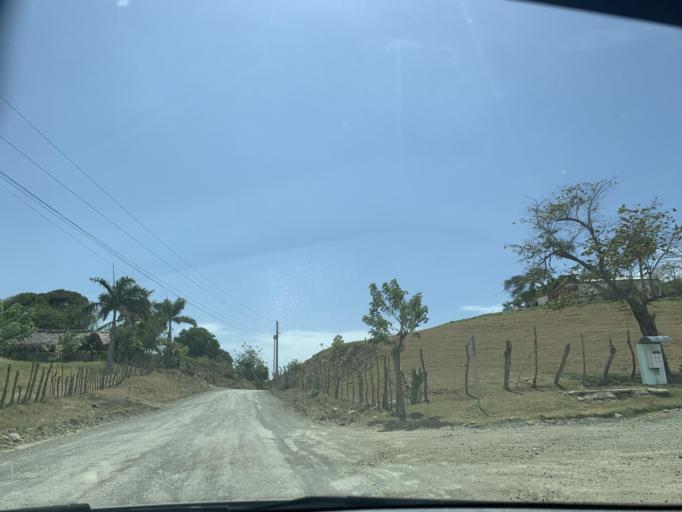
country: DO
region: Puerto Plata
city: Imbert
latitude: 19.8673
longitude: -70.8167
